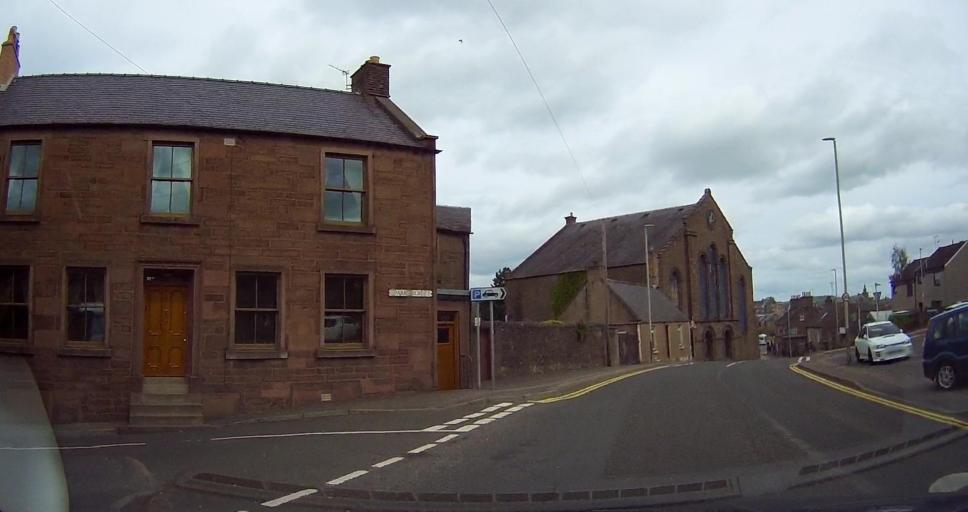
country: GB
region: Scotland
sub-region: Angus
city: Forfar
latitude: 56.6431
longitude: -2.8857
